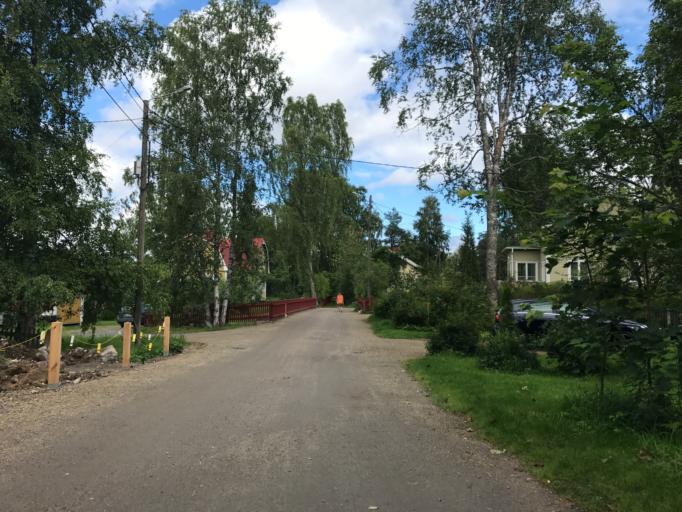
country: FI
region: Pirkanmaa
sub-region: Etelae-Pirkanmaa
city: Valkeakoski
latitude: 61.2670
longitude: 24.0374
